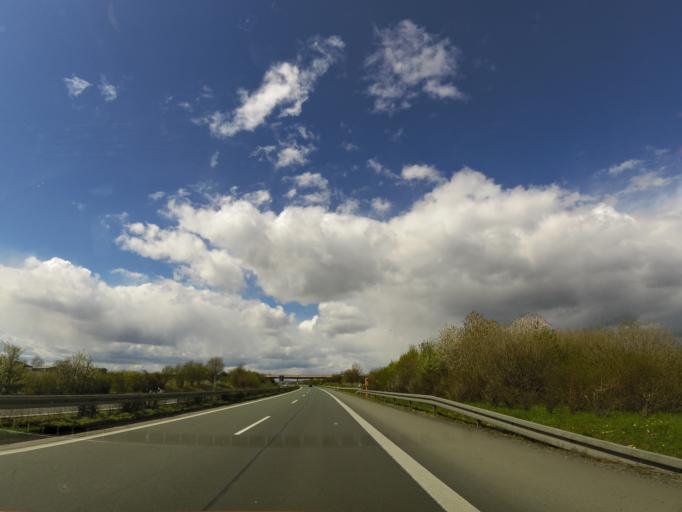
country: DE
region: Saxony-Anhalt
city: Stapelburg
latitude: 51.9331
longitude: 10.6410
